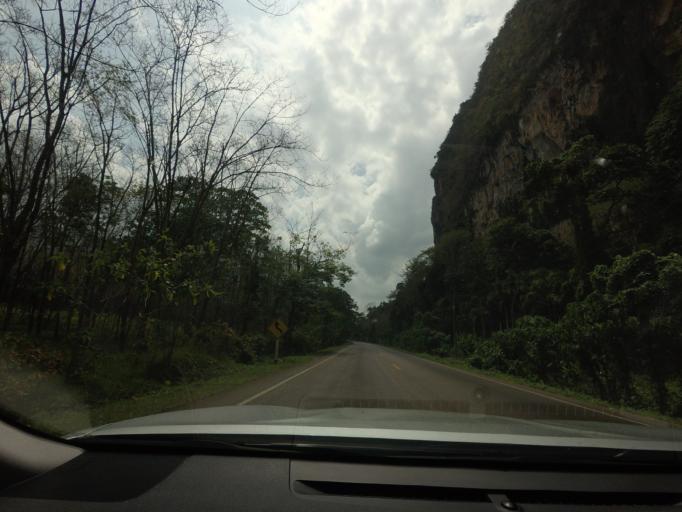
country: TH
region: Phangnga
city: Ban Ao Nang
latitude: 8.1327
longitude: 98.8067
